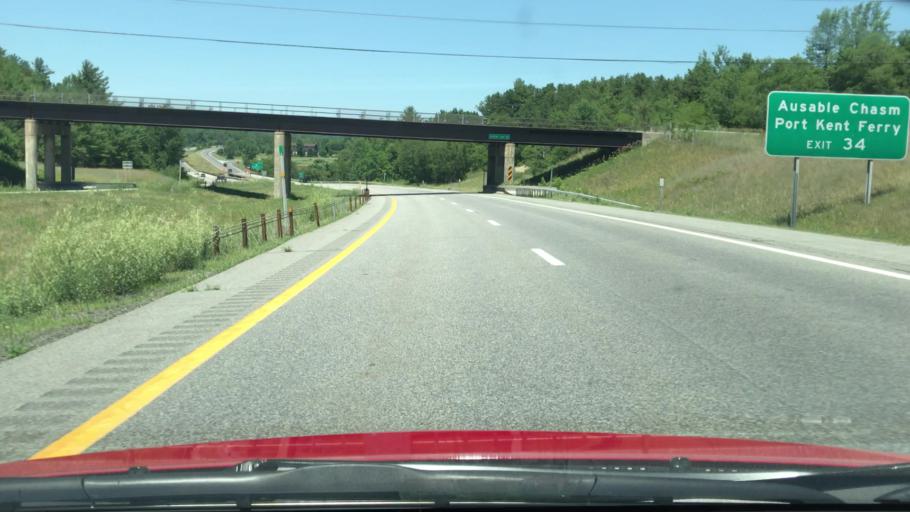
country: US
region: New York
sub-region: Essex County
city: Keeseville
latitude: 44.4880
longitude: -73.4904
